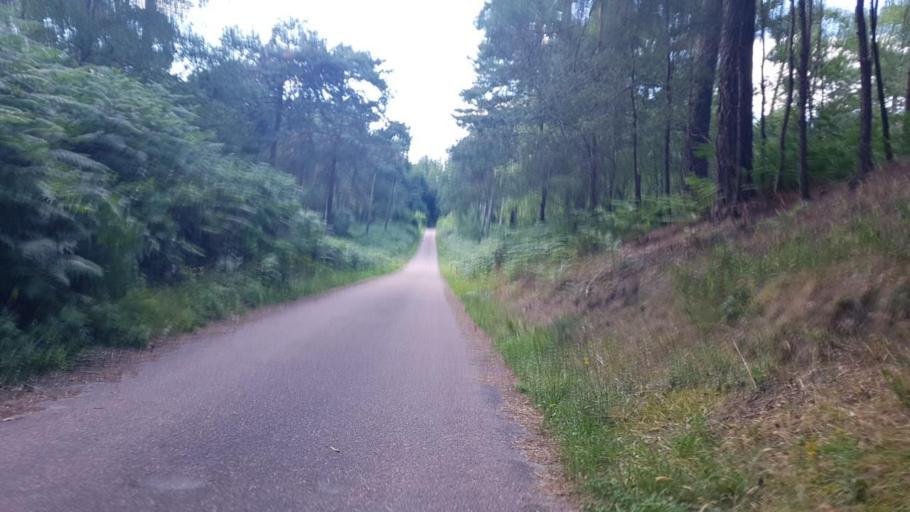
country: FR
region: Picardie
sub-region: Departement de l'Oise
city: Thiers-sur-Theve
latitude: 49.1548
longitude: 2.6381
